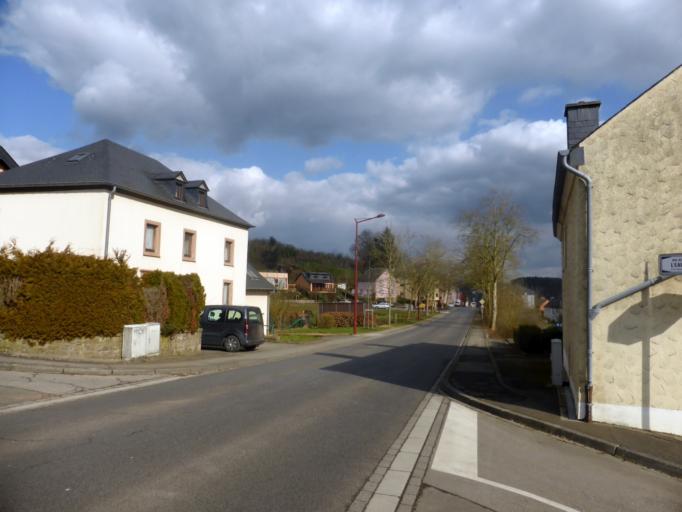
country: LU
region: Luxembourg
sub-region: Canton de Mersch
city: Bissen
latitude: 49.7865
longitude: 6.0587
